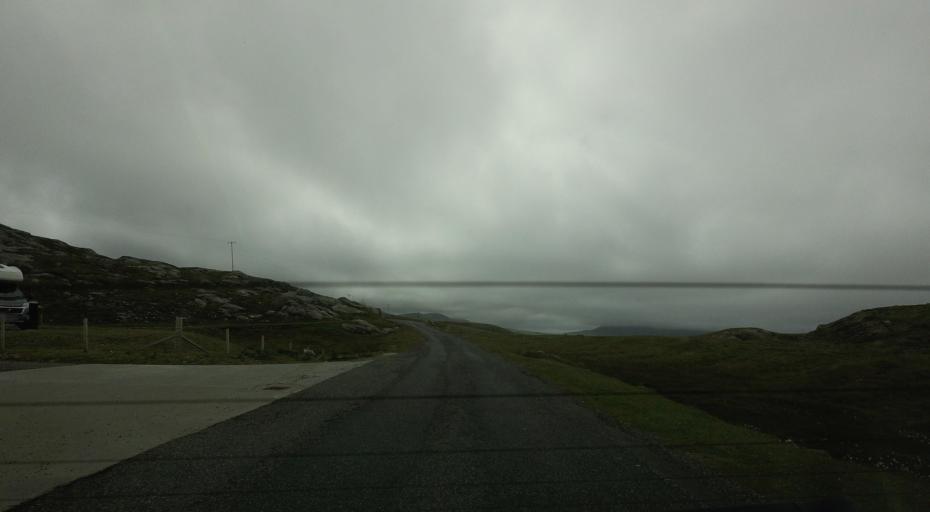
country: GB
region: Scotland
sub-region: Eilean Siar
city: Harris
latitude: 57.8572
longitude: -6.9976
